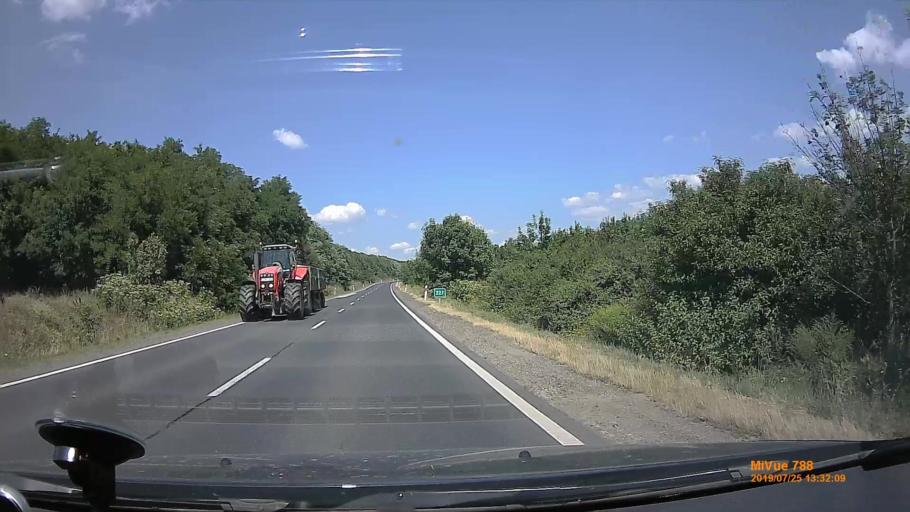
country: HU
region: Borsod-Abauj-Zemplen
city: Encs
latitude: 48.3728
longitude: 21.1437
